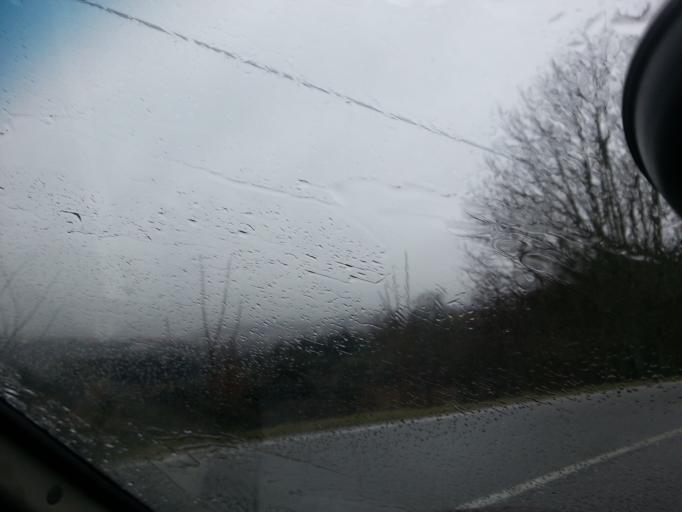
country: PT
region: Viseu
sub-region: Mangualde
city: Mangualde
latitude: 40.6080
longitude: -7.6874
